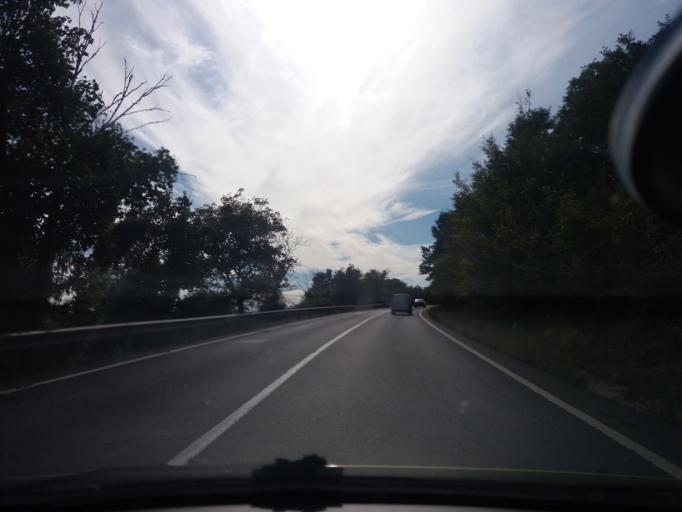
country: RO
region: Hunedoara
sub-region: Comuna Dobra
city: Dobra
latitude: 45.9408
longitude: 22.5658
